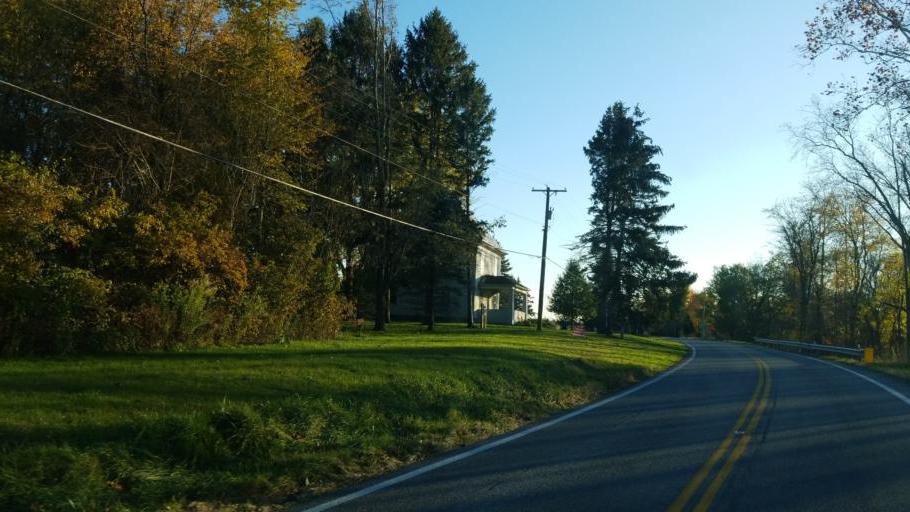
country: US
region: Ohio
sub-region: Sandusky County
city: Green Springs
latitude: 41.3224
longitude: -83.0562
